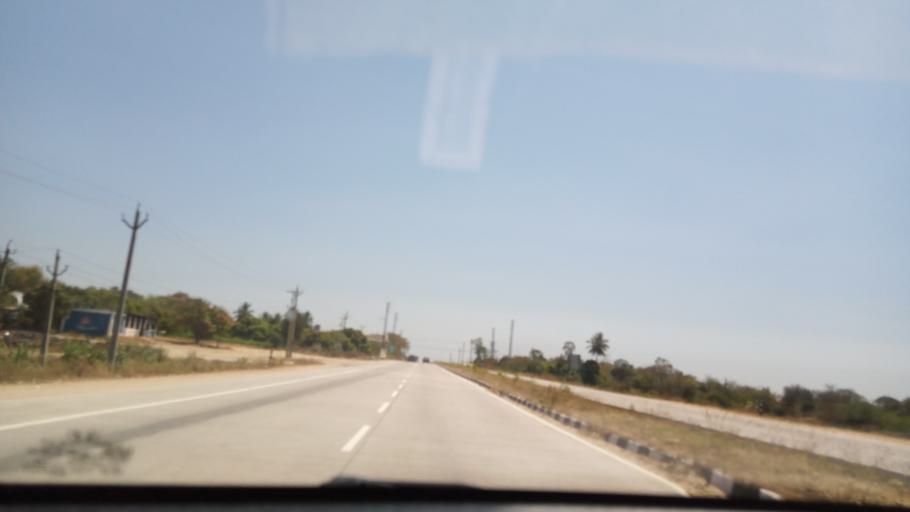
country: IN
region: Andhra Pradesh
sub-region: Chittoor
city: Chittoor
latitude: 13.1982
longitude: 78.9757
